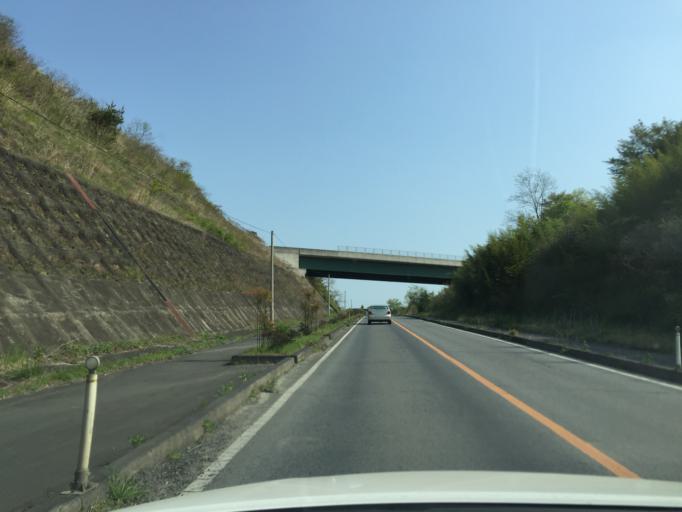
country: JP
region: Fukushima
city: Iwaki
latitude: 37.1056
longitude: 140.8758
